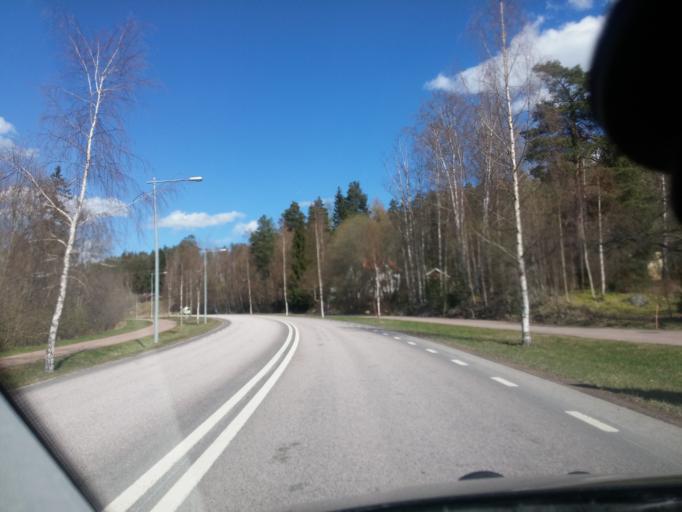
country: SE
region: Dalarna
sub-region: Faluns Kommun
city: Falun
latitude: 60.6305
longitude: 15.6223
